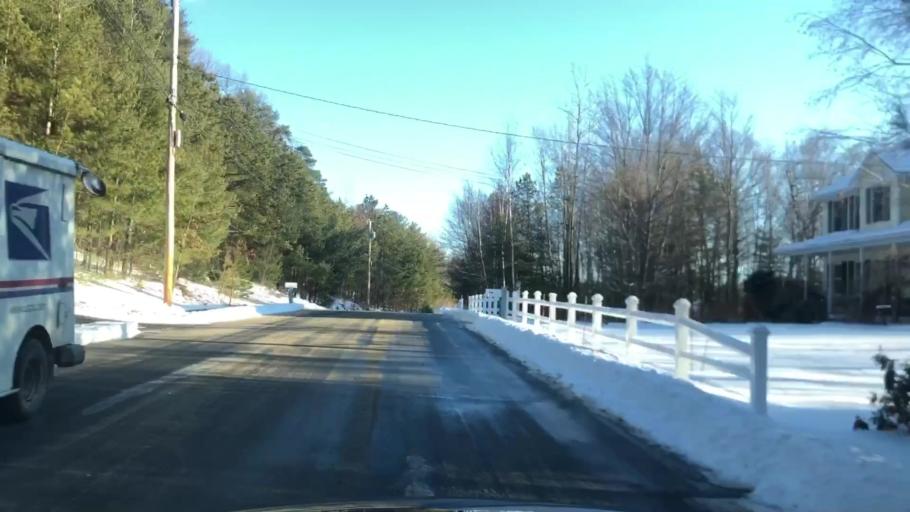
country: US
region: New Hampshire
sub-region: Hillsborough County
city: Milford
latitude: 42.8016
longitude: -71.6702
